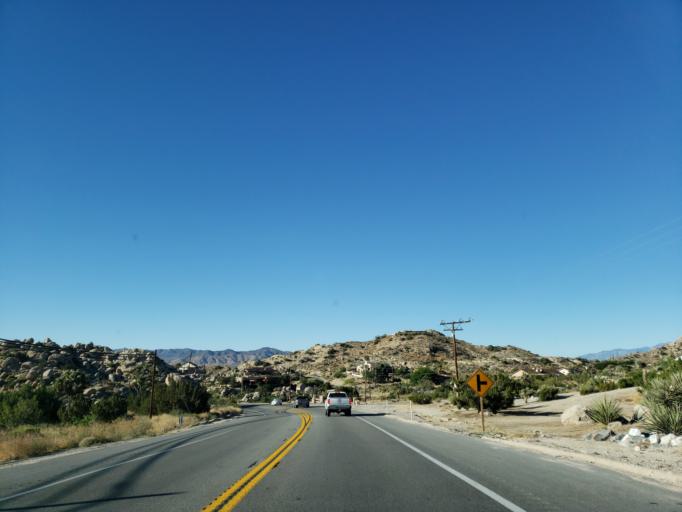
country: US
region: California
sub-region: San Bernardino County
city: Yucca Valley
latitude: 34.1489
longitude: -116.4190
